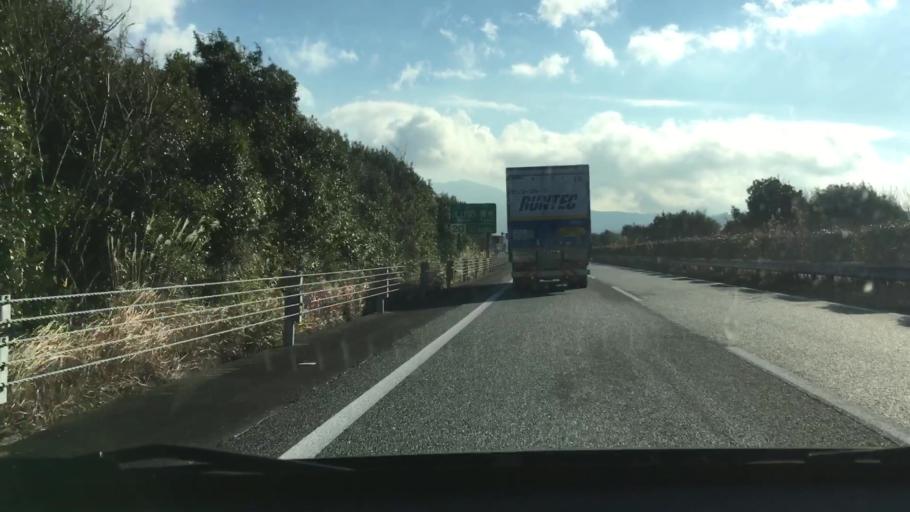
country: JP
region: Kumamoto
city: Hitoyoshi
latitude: 32.0579
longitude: 130.8029
